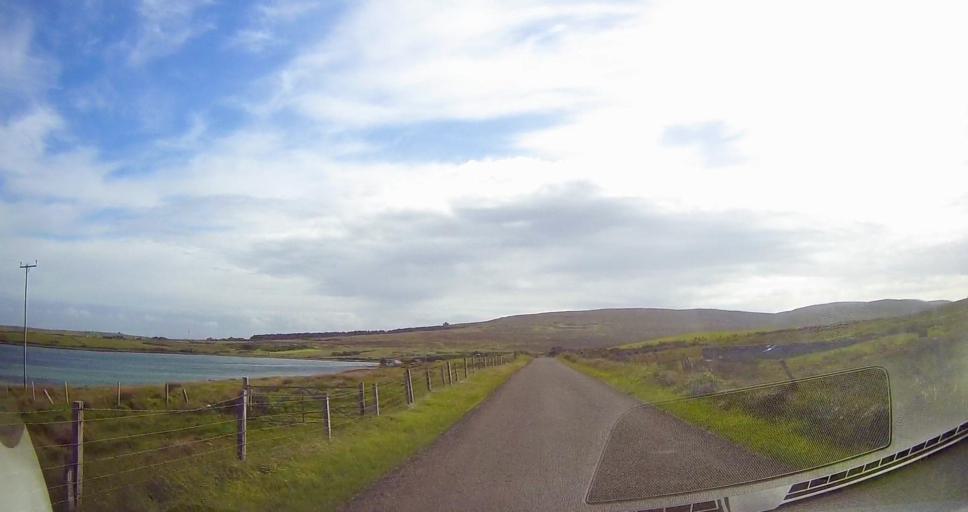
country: GB
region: Scotland
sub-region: Orkney Islands
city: Stromness
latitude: 58.8462
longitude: -3.2066
